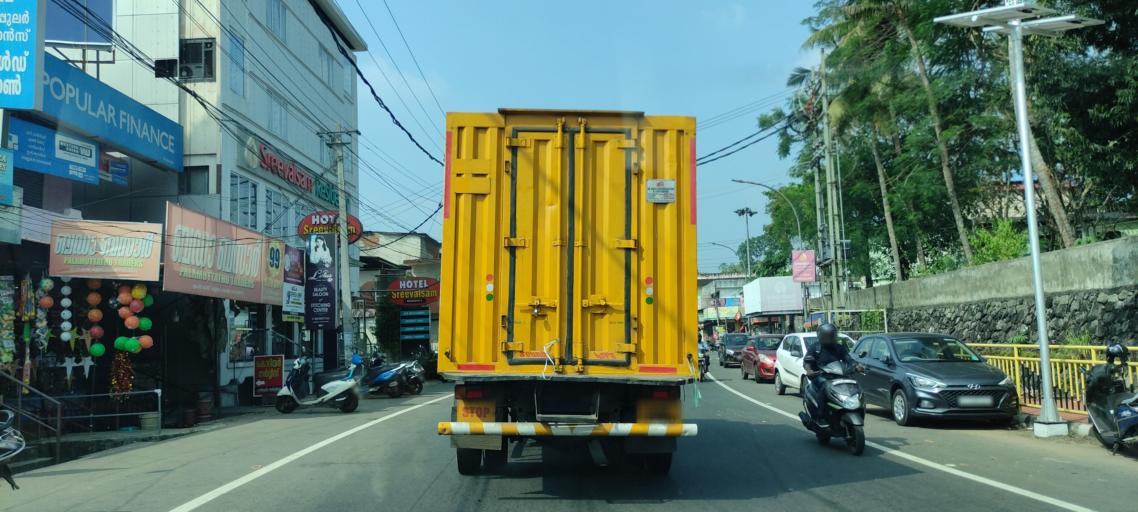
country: IN
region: Kerala
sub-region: Alappuzha
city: Chengannur
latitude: 9.2423
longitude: 76.6723
